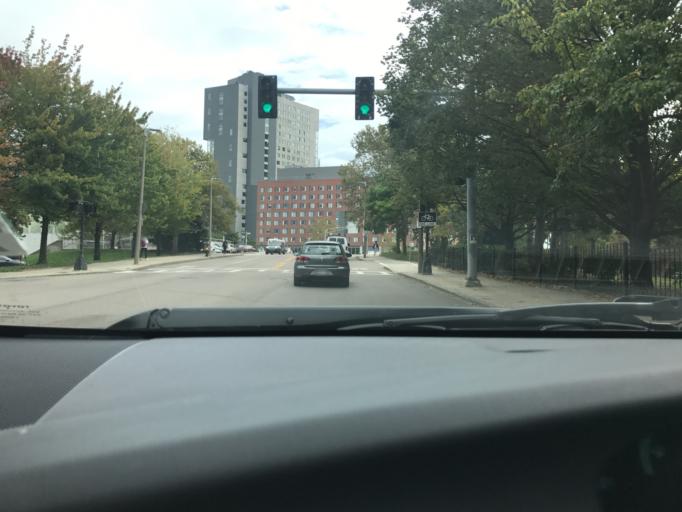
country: US
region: Massachusetts
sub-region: Norfolk County
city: Brookline
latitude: 42.3361
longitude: -71.0915
